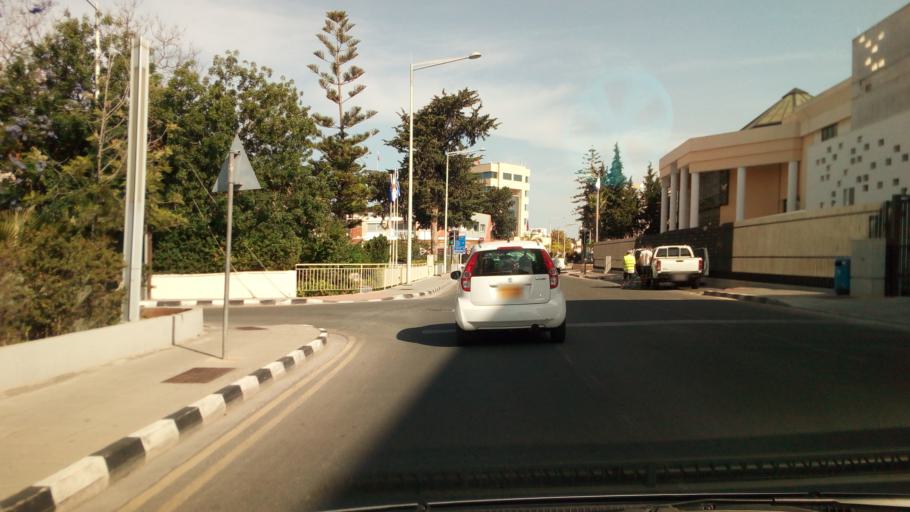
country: CY
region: Pafos
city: Paphos
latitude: 34.7750
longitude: 32.4272
